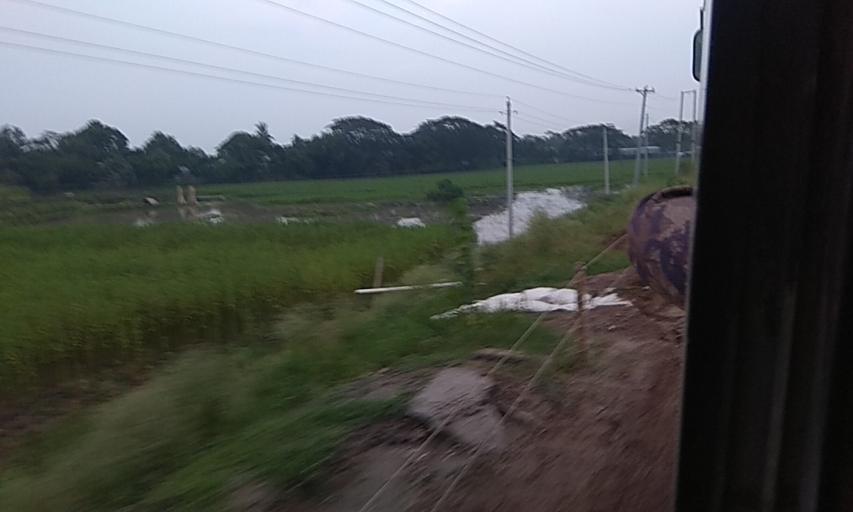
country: BD
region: Dhaka
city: Char Bhadrasan
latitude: 23.3820
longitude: 90.0031
